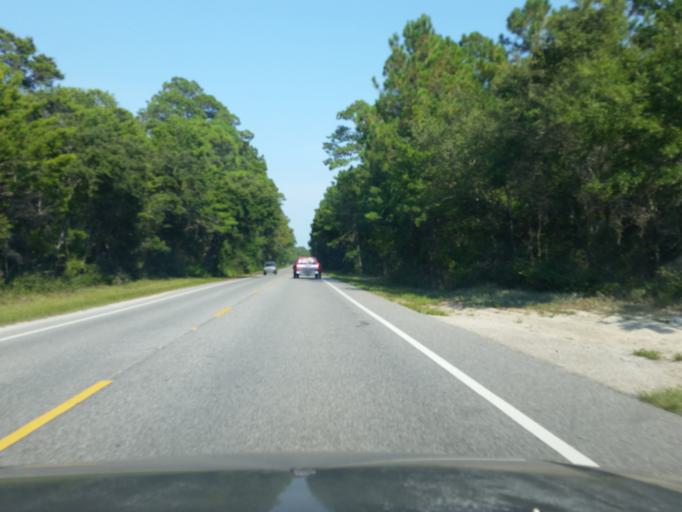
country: US
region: Alabama
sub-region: Baldwin County
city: Gulf Shores
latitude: 30.2500
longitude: -87.7980
